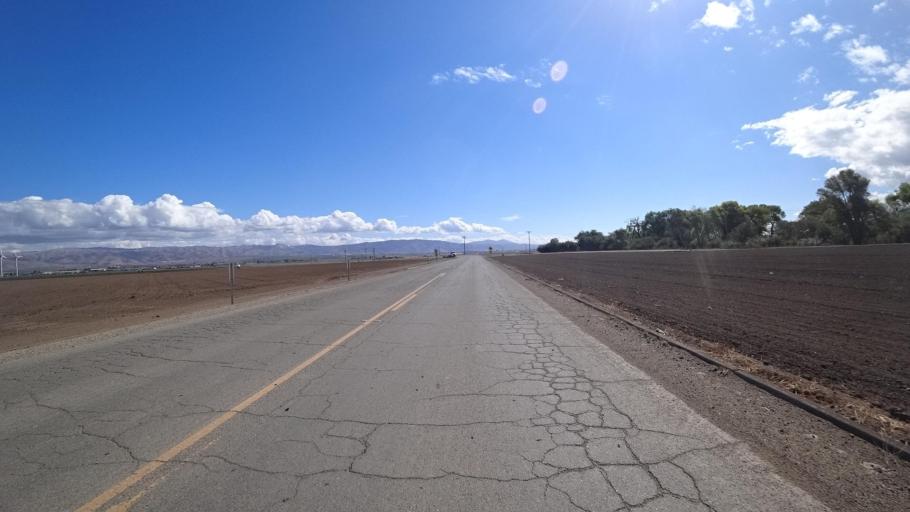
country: US
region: California
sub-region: Monterey County
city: Gonzales
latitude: 36.4896
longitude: -121.4661
